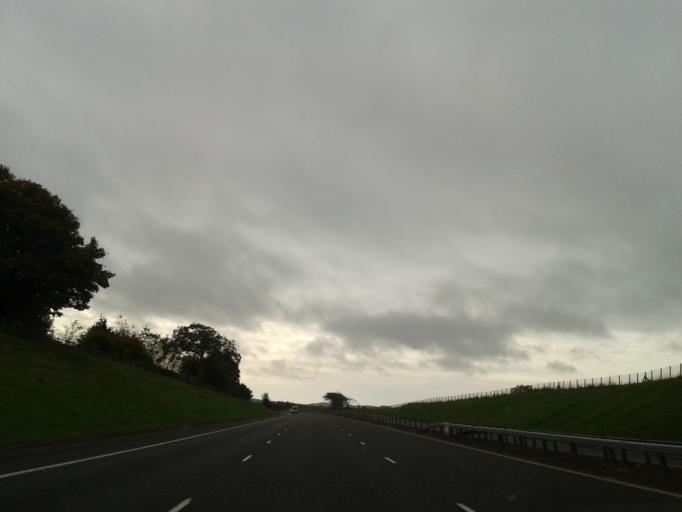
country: GB
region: Scotland
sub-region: Dumfries and Galloway
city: Lockerbie
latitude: 55.1092
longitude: -3.3546
